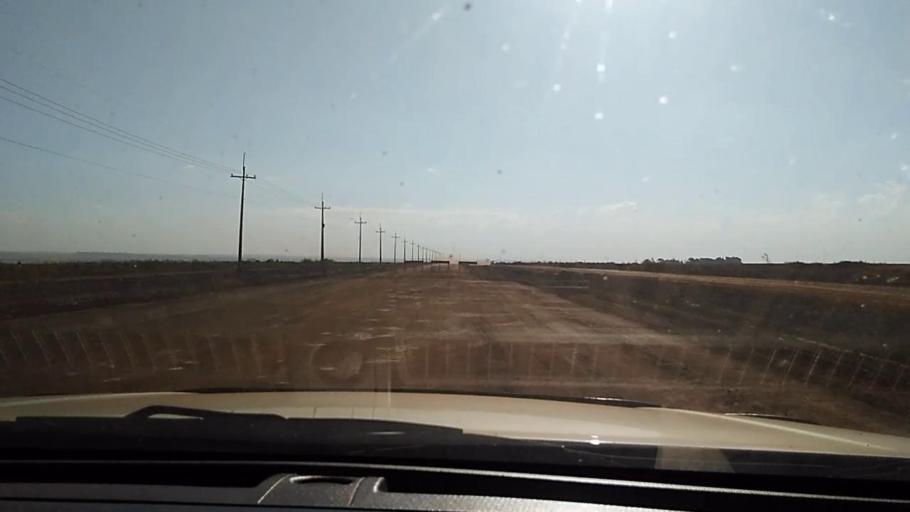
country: PY
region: Alto Parana
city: Naranjal
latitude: -25.9181
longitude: -55.4287
